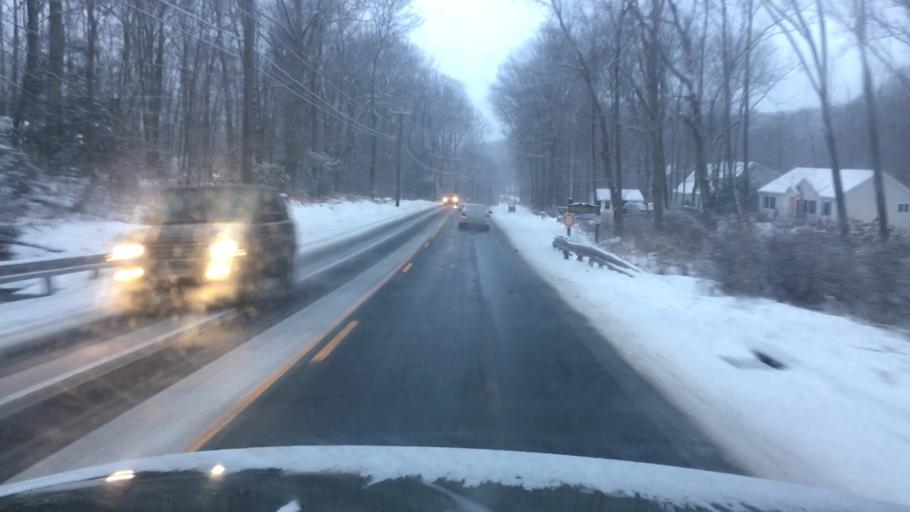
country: US
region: Connecticut
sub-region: Tolland County
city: Somers
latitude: 41.9805
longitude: -72.4068
